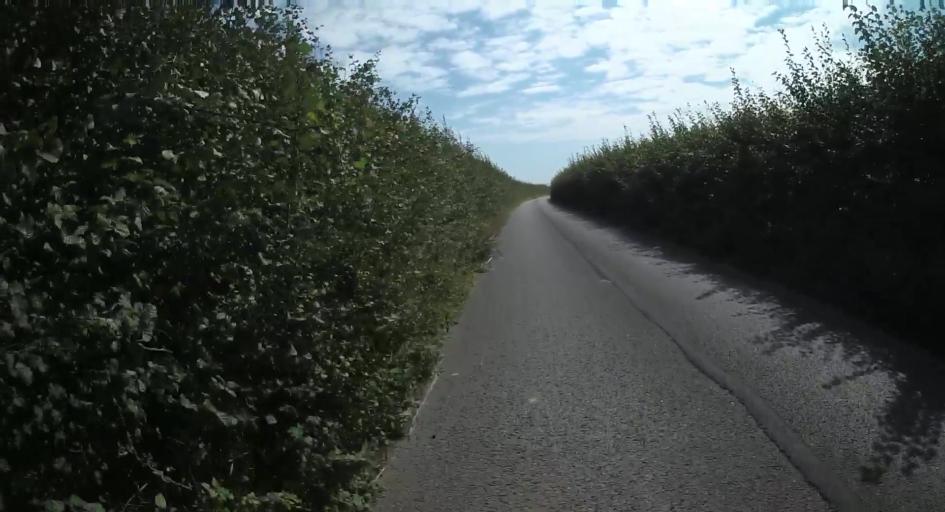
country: GB
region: England
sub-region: Isle of Wight
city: Chale
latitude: 50.6257
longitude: -1.3689
